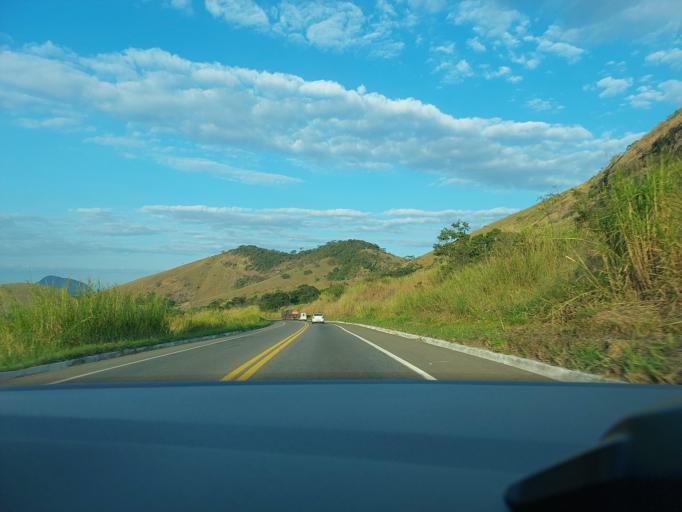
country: BR
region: Minas Gerais
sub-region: Muriae
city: Muriae
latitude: -21.1269
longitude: -42.2456
